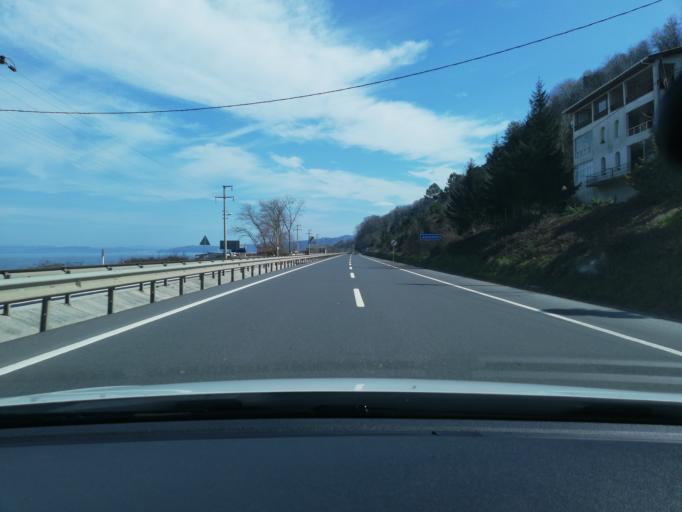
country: TR
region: Duzce
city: Akcakoca
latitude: 41.0956
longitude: 31.2007
